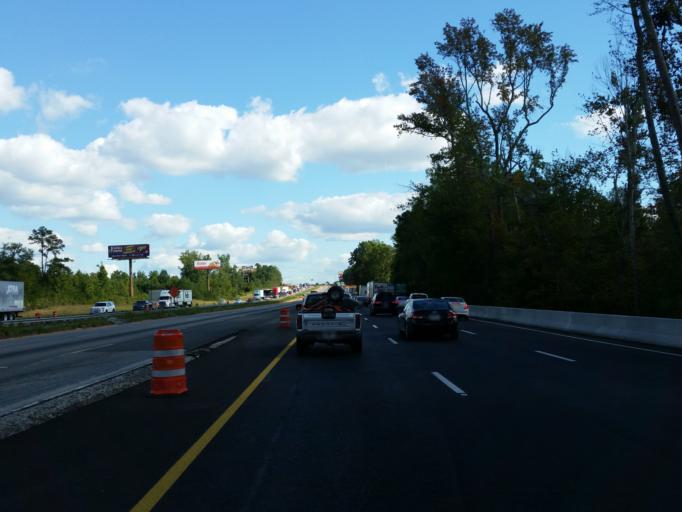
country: US
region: Georgia
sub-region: Henry County
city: McDonough
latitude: 33.4383
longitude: -84.1924
